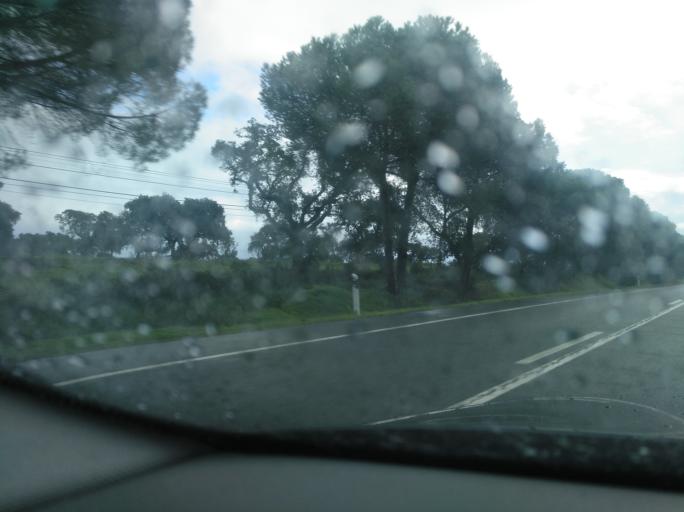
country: PT
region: Setubal
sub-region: Grandola
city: Grandola
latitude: 38.0813
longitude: -8.4171
